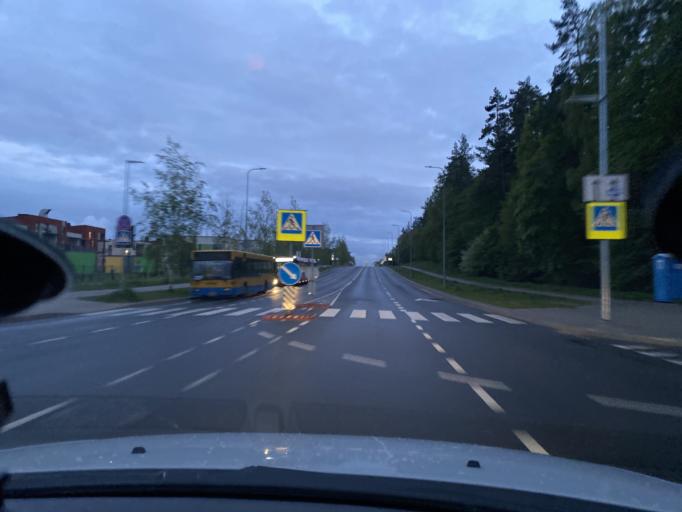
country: LT
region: Vilnius County
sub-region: Vilnius
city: Fabijoniskes
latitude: 54.7632
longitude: 25.2821
